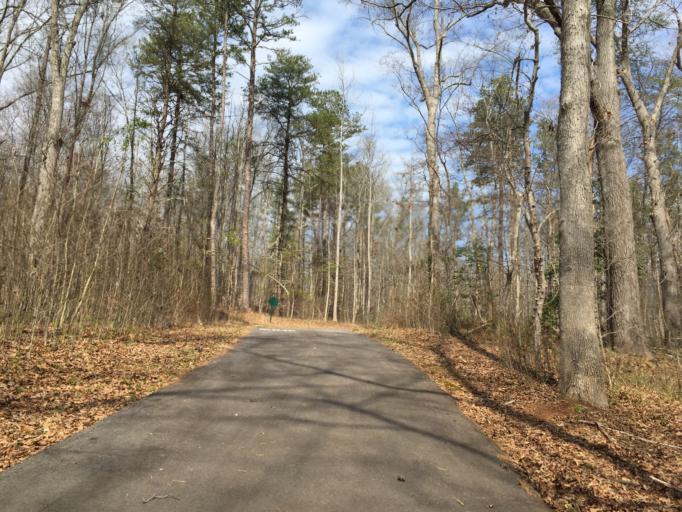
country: US
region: South Carolina
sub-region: Greenville County
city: Mauldin
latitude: 34.7883
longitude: -82.3643
